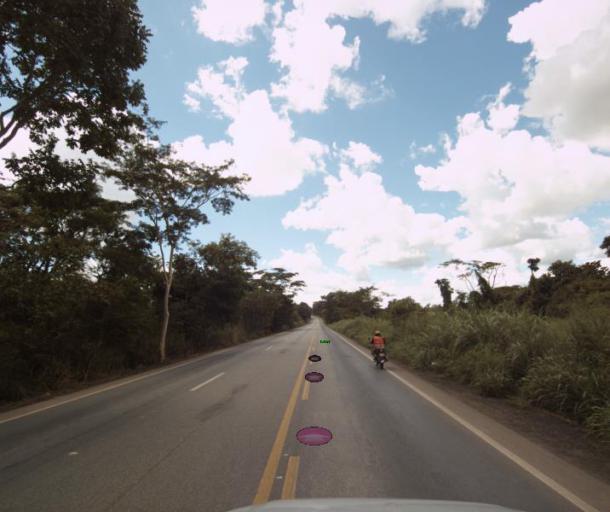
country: BR
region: Goias
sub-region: Porangatu
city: Porangatu
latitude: -13.7654
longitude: -49.0291
